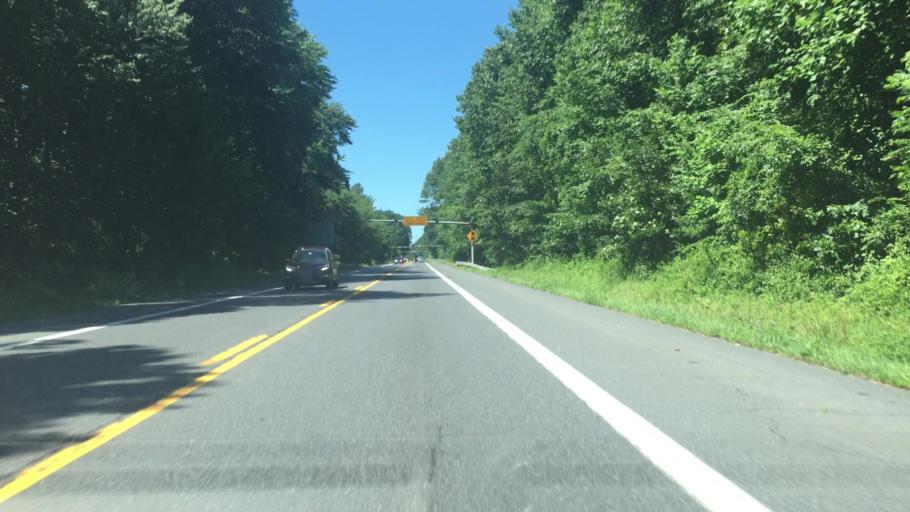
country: US
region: Maryland
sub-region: Howard County
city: Highland
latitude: 39.2463
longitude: -76.9778
